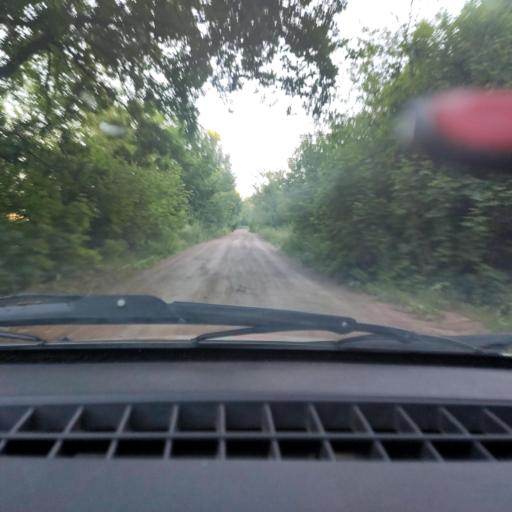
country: RU
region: Bashkortostan
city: Karmaskaly
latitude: 54.3725
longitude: 55.9110
